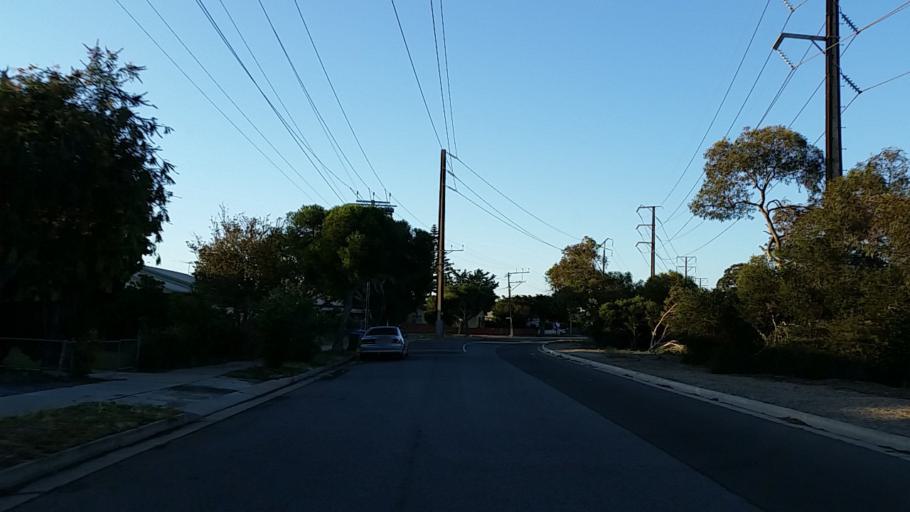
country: AU
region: South Australia
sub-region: Port Adelaide Enfield
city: Birkenhead
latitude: -34.8034
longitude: 138.5053
